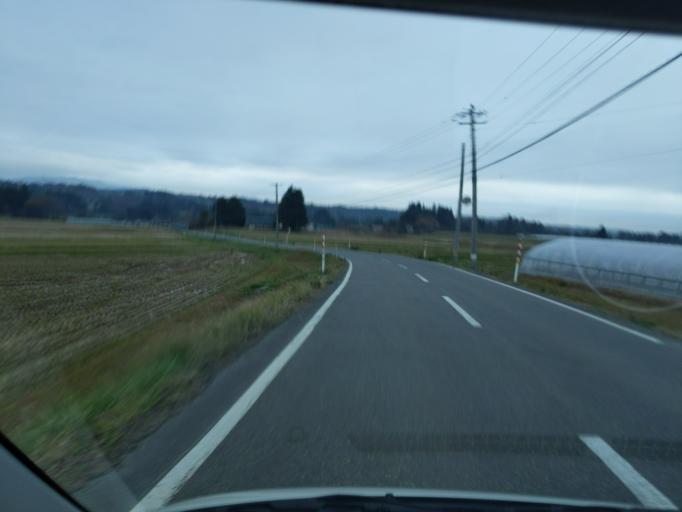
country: JP
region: Iwate
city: Kitakami
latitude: 39.2297
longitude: 141.2359
